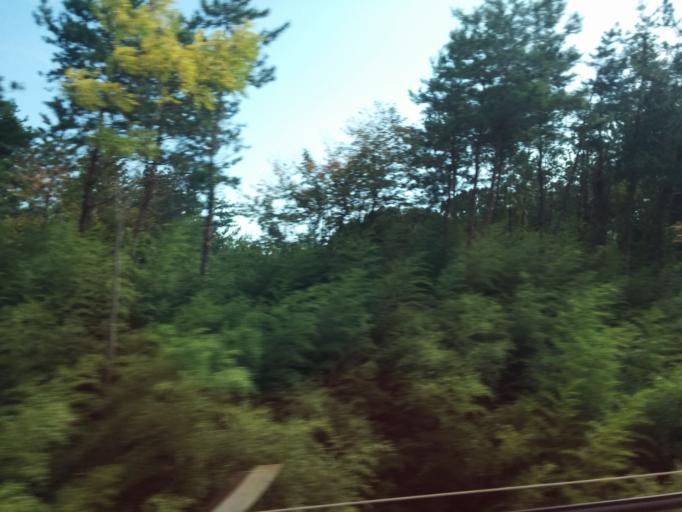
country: JP
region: Shiga Prefecture
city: Kusatsu
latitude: 34.9963
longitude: 135.9590
